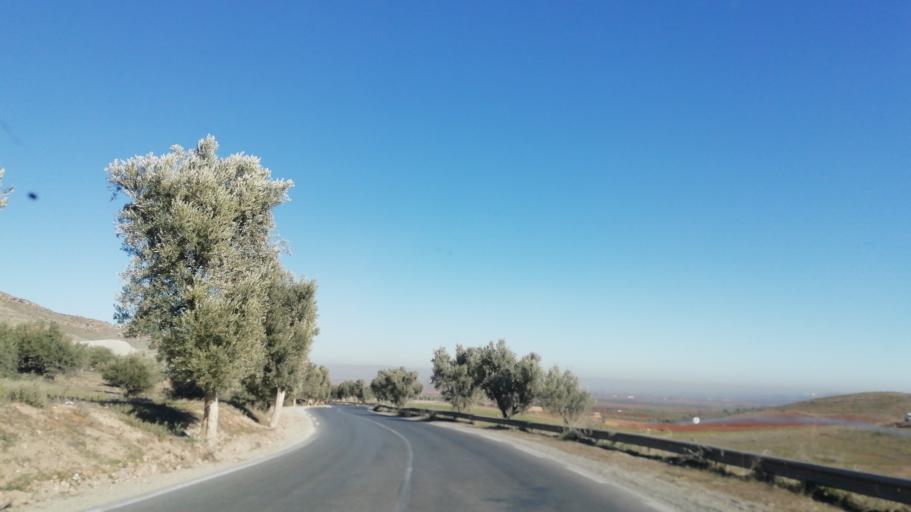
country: DZ
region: Mascara
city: Mascara
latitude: 35.2483
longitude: 0.1212
